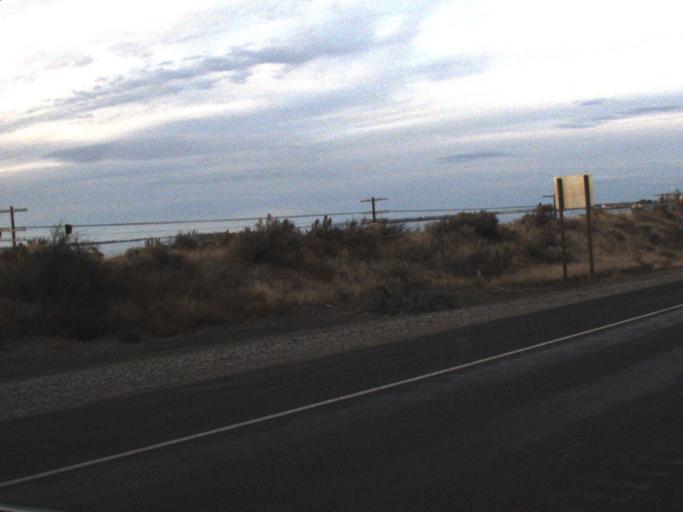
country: US
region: Washington
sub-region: Benton County
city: Finley
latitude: 46.0753
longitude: -118.9078
